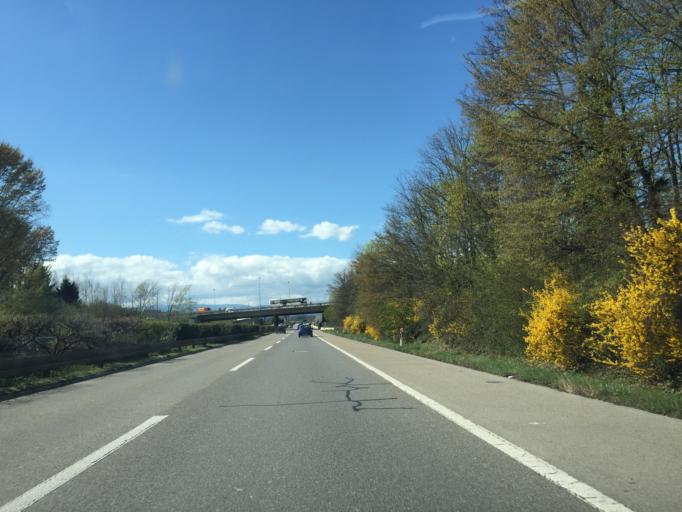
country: CH
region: Vaud
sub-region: Ouest Lausannois District
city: Prilly
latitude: 46.5217
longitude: 6.5911
